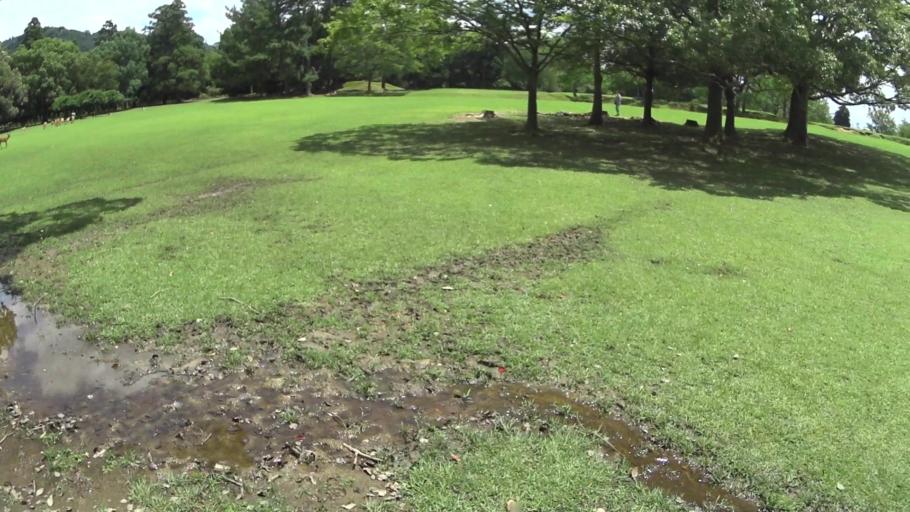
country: JP
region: Nara
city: Nara-shi
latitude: 34.6815
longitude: 135.8407
